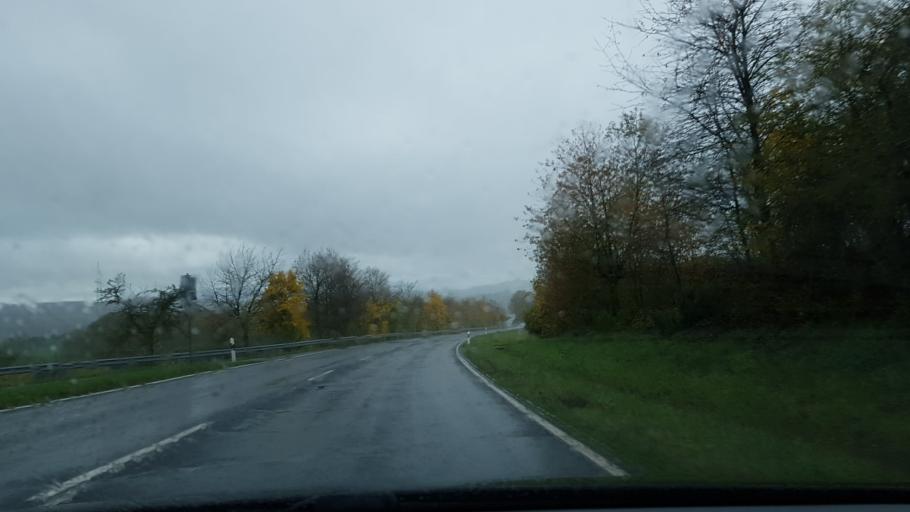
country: DE
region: Rheinland-Pfalz
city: Salmtal
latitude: 49.9382
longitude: 6.8507
